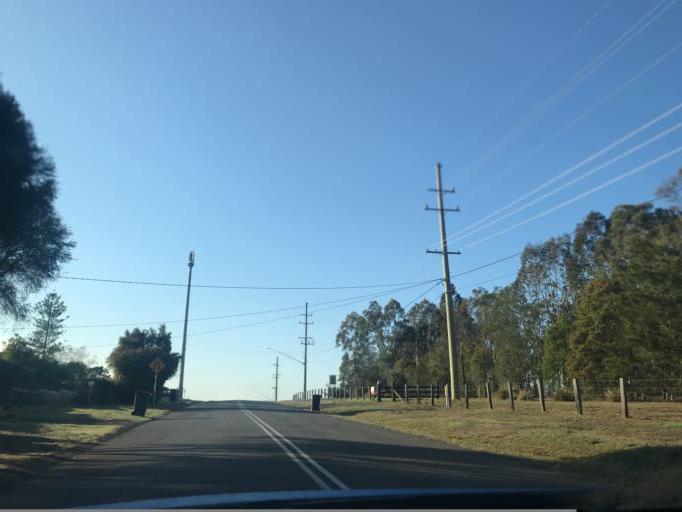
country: AU
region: New South Wales
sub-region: Cessnock
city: Cessnock
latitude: -32.9057
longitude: 151.2838
